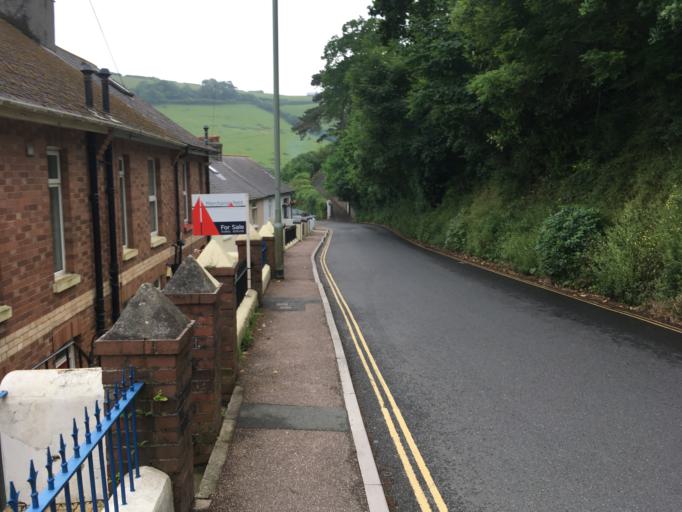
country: GB
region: England
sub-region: Devon
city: Dartmouth
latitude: 50.3508
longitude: -3.5887
